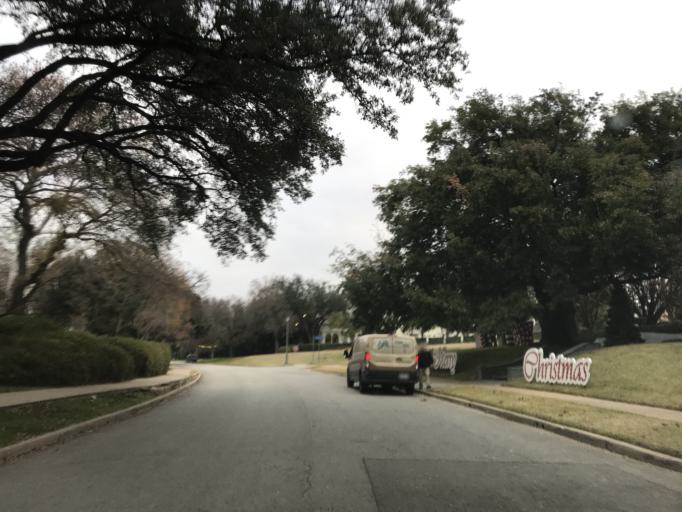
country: US
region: Texas
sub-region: Dallas County
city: Highland Park
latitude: 32.8243
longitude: -96.8003
